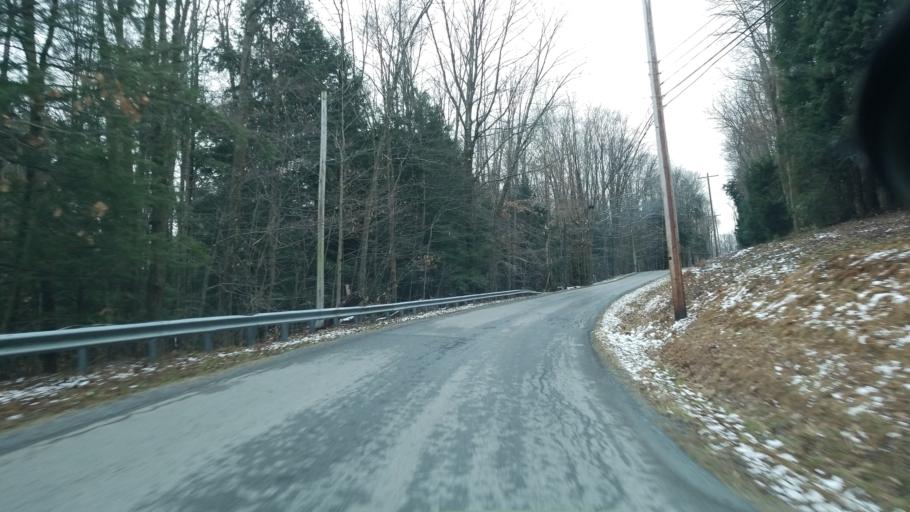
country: US
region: Pennsylvania
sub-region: Clearfield County
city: Treasure Lake
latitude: 41.0983
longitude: -78.6369
